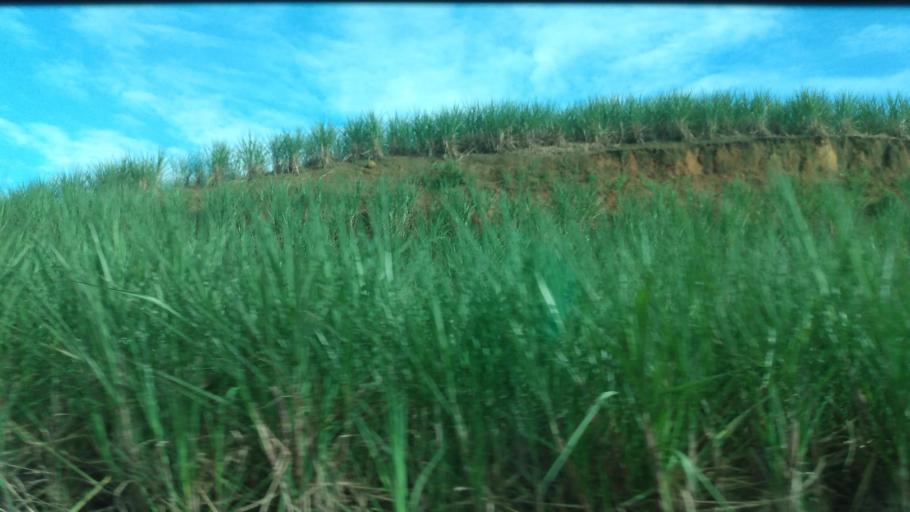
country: BR
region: Pernambuco
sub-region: Palmares
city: Palmares
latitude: -8.6945
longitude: -35.6529
